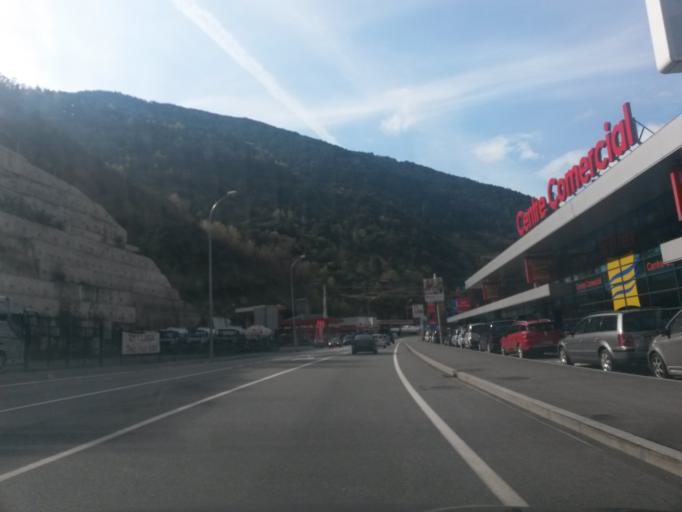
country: AD
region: Sant Julia de Loria
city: Sant Julia de Loria
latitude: 42.4546
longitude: 1.4869
